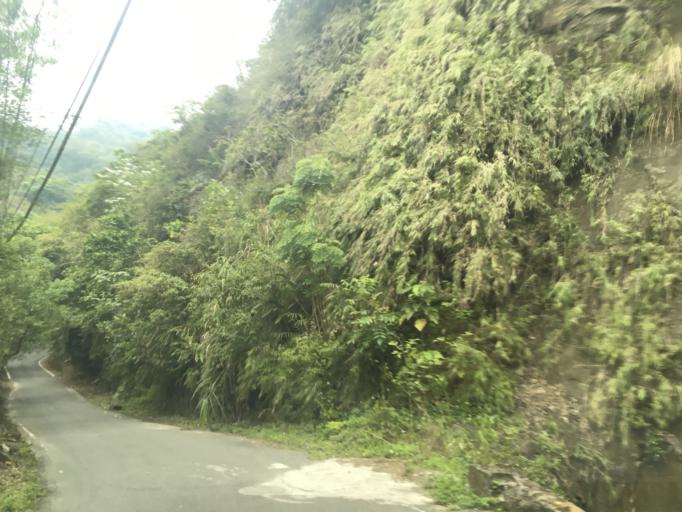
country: TW
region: Taiwan
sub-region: Taichung City
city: Taichung
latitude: 24.0577
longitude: 120.7714
